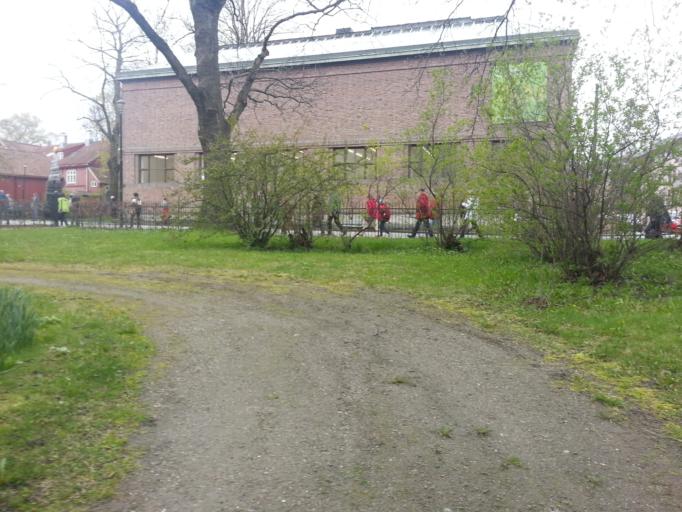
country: NO
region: Sor-Trondelag
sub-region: Trondheim
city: Trondheim
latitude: 63.4275
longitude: 10.3956
